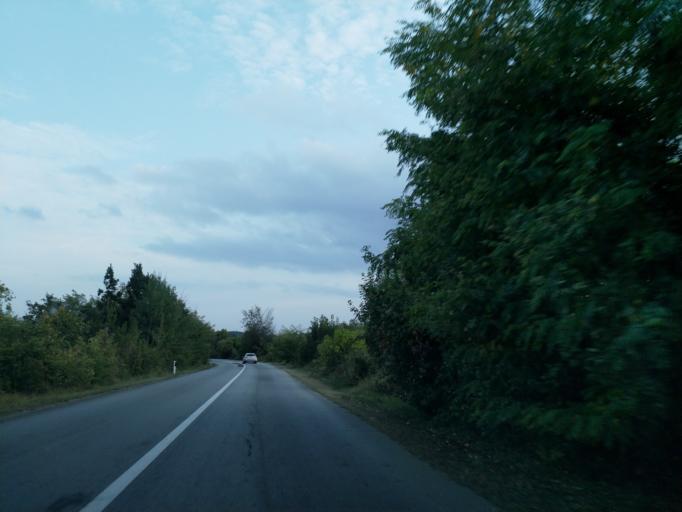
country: RS
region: Central Serbia
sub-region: Sumadijski Okrug
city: Topola
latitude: 44.1549
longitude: 20.7401
